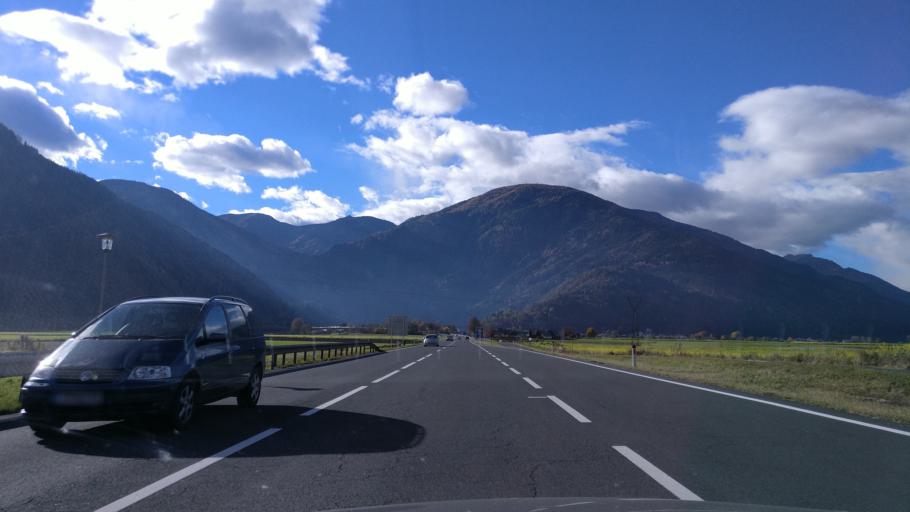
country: AT
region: Carinthia
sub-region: Politischer Bezirk Spittal an der Drau
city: Lendorf
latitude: 46.8327
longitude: 13.3953
